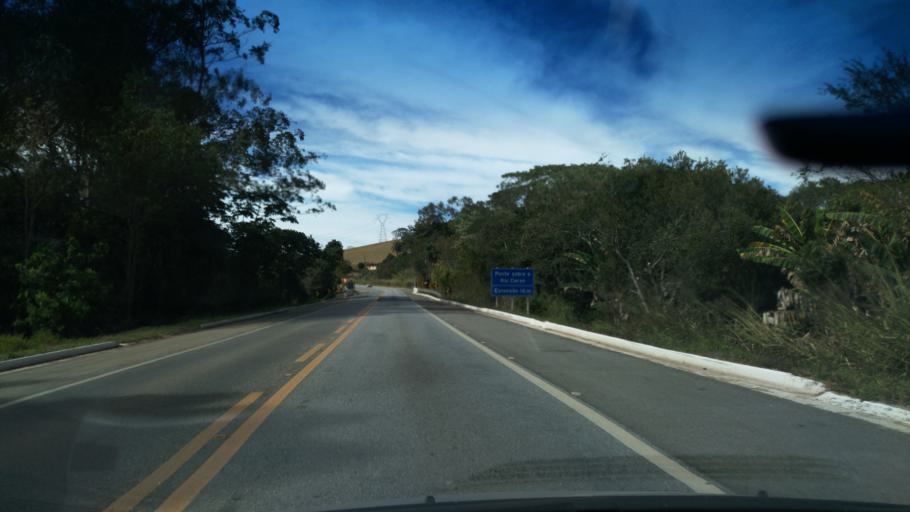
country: BR
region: Minas Gerais
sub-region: Borda Da Mata
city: Borda da Mata
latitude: -22.1581
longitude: -46.1152
